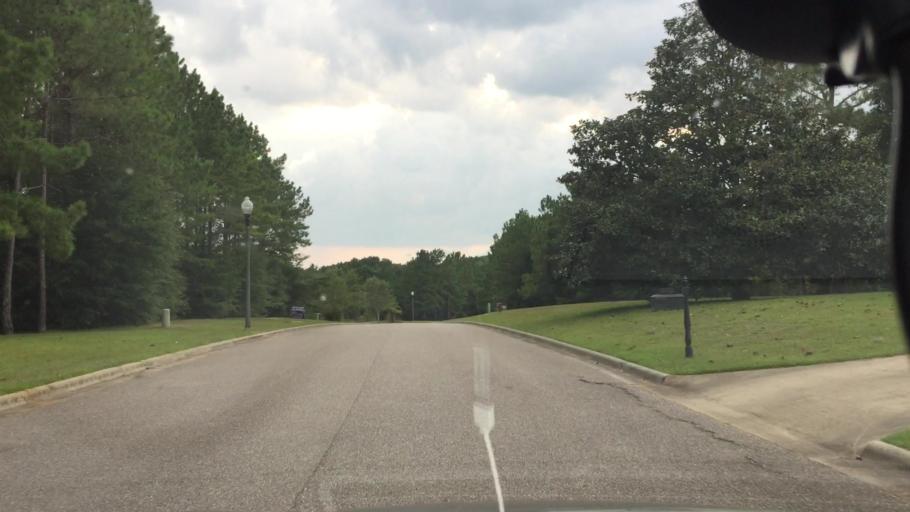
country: US
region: Alabama
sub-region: Coffee County
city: Enterprise
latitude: 31.3633
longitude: -85.8313
